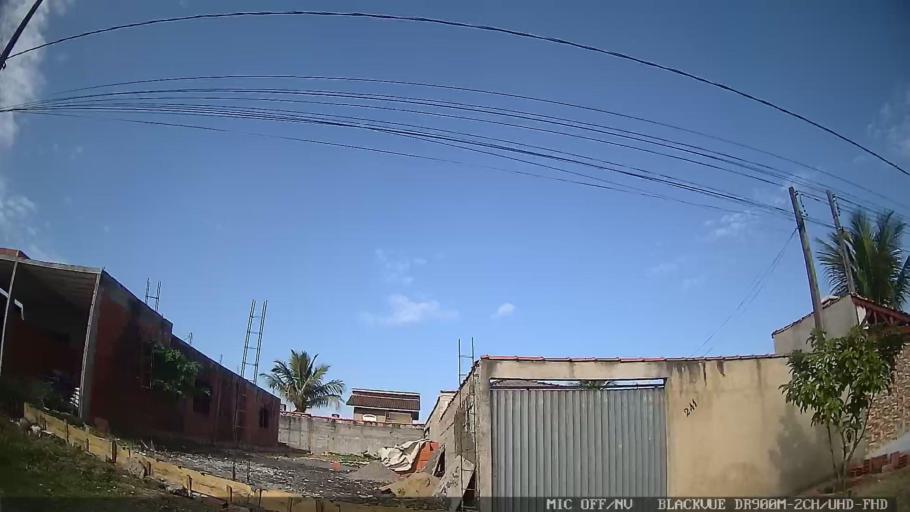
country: BR
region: Sao Paulo
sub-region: Guaruja
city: Guaruja
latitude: -23.9764
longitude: -46.2149
